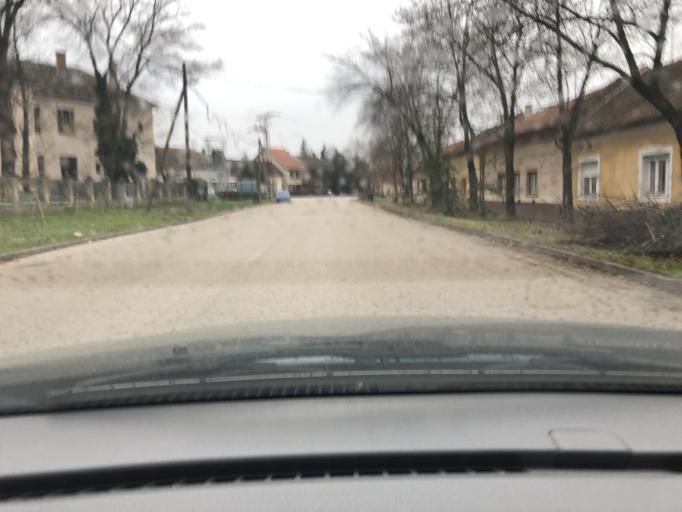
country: HU
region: Csongrad
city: Csongrad
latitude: 46.7052
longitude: 20.1466
